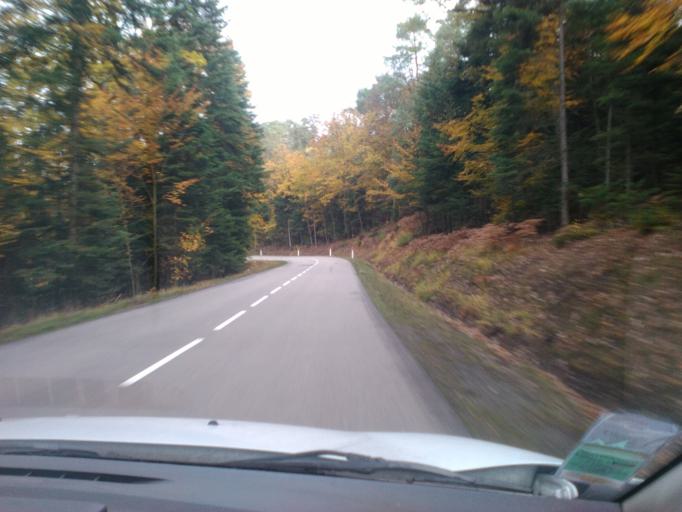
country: FR
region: Lorraine
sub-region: Departement des Vosges
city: Etival-Clairefontaine
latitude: 48.3755
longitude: 6.7858
